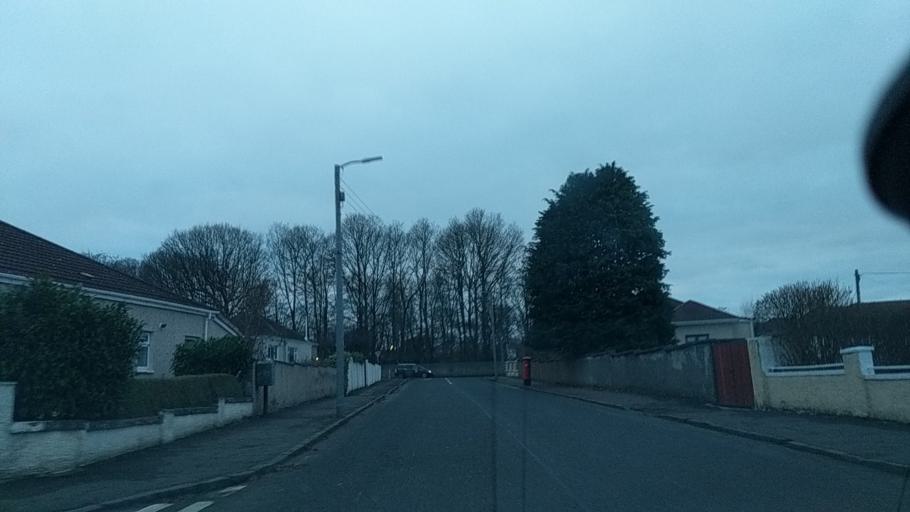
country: GB
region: Scotland
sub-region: South Lanarkshire
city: Rutherglen
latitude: 55.8232
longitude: -4.1969
